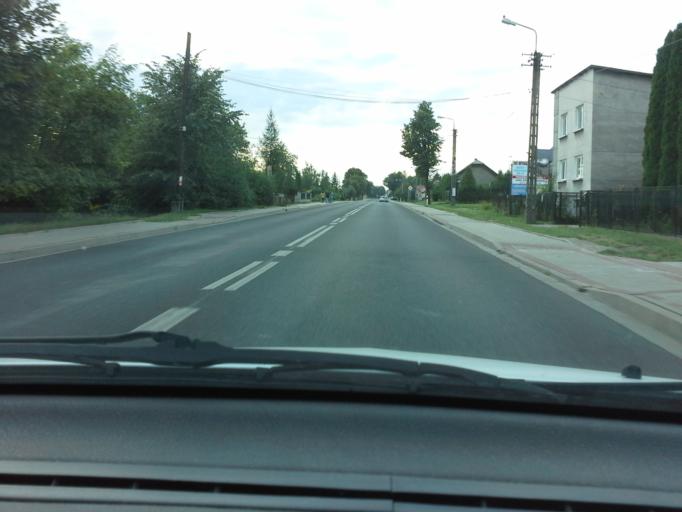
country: PL
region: Lesser Poland Voivodeship
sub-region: Powiat chrzanowski
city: Trzebinia
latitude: 50.1528
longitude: 19.4862
